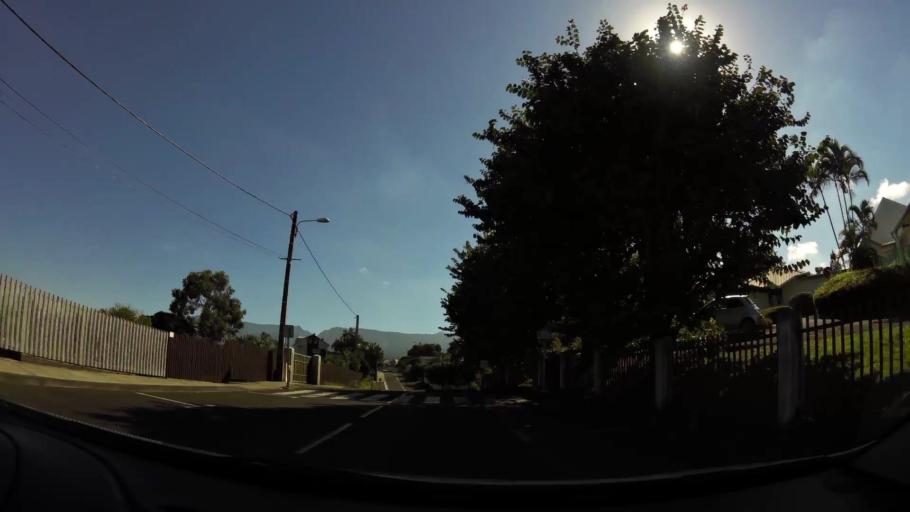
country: RE
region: Reunion
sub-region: Reunion
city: Le Tampon
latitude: -21.2760
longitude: 55.5155
